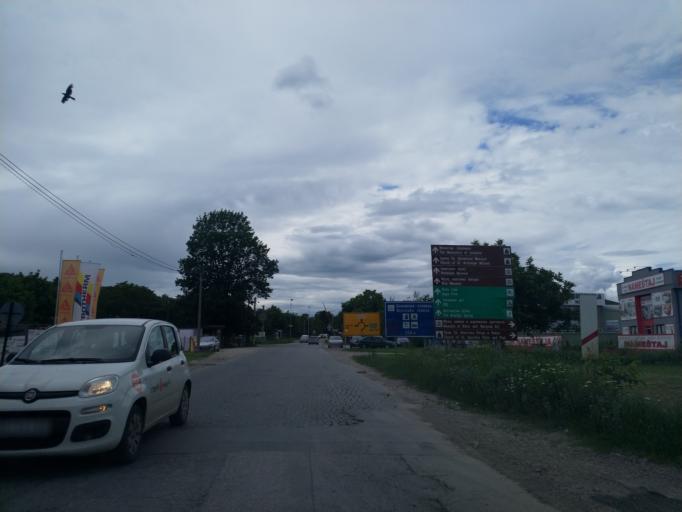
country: RS
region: Central Serbia
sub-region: Pomoravski Okrug
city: Jagodina
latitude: 43.9619
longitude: 21.2813
